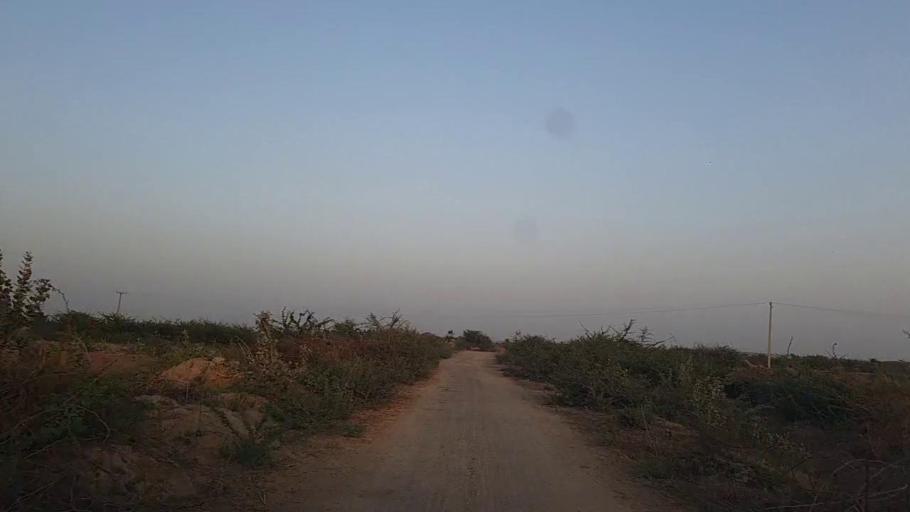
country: PK
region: Sindh
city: Naukot
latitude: 24.6948
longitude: 69.2820
